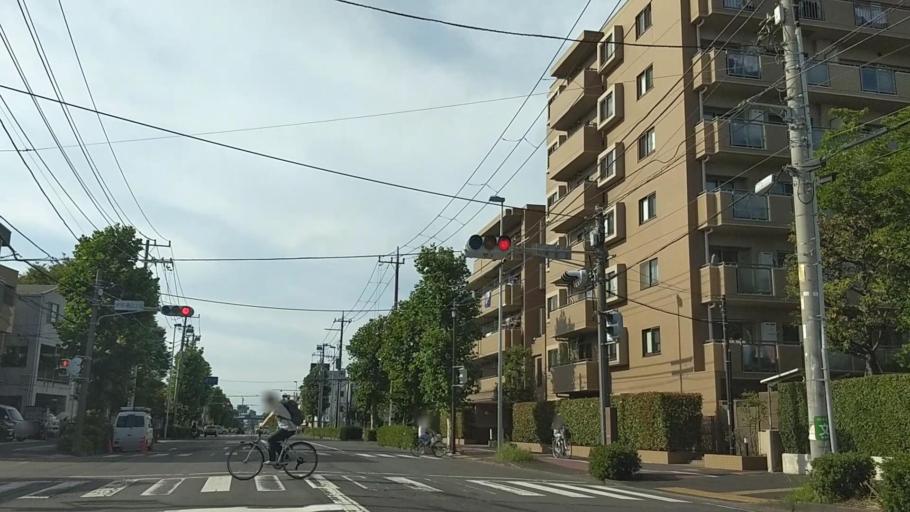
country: JP
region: Kanagawa
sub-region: Kawasaki-shi
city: Kawasaki
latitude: 35.5091
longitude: 139.6922
